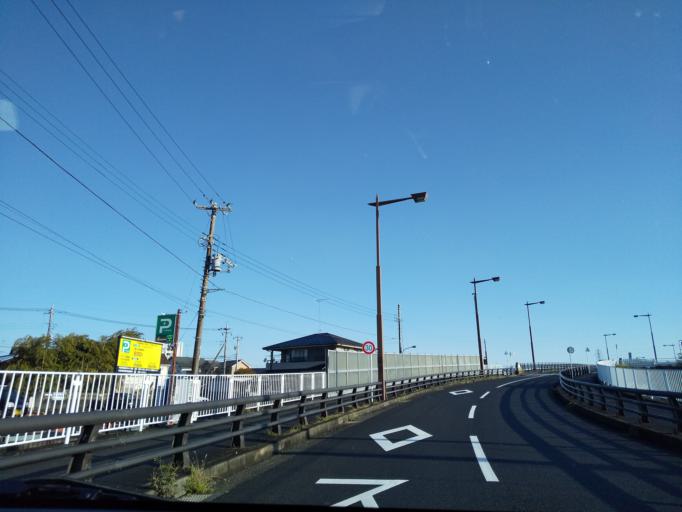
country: JP
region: Tokyo
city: Hachioji
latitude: 35.6438
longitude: 139.3664
